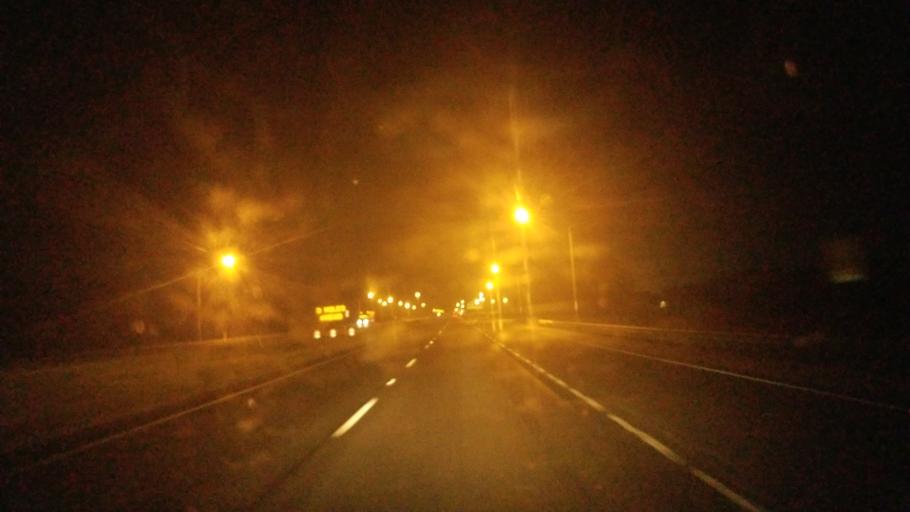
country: US
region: Indiana
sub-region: Vigo County
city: Seelyville
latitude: 39.4308
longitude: -87.3185
